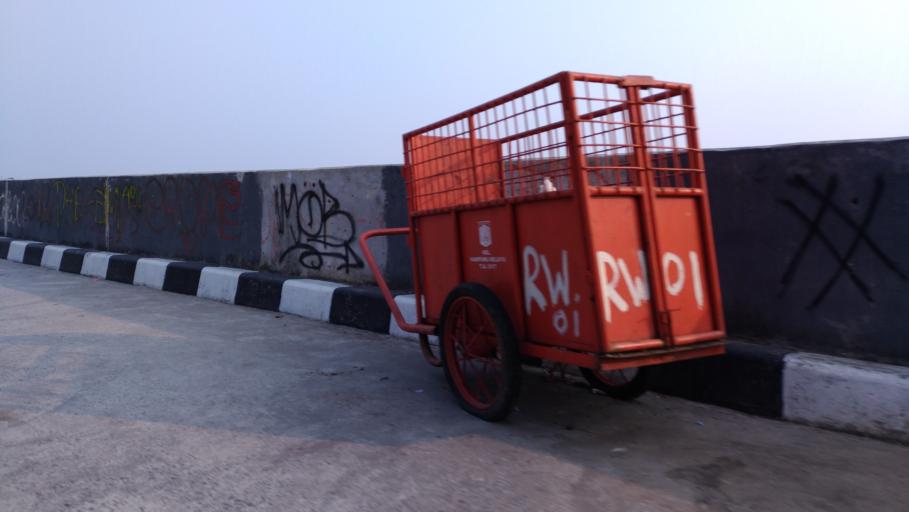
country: ID
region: Jakarta Raya
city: Jakarta
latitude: -6.2220
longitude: 106.8643
